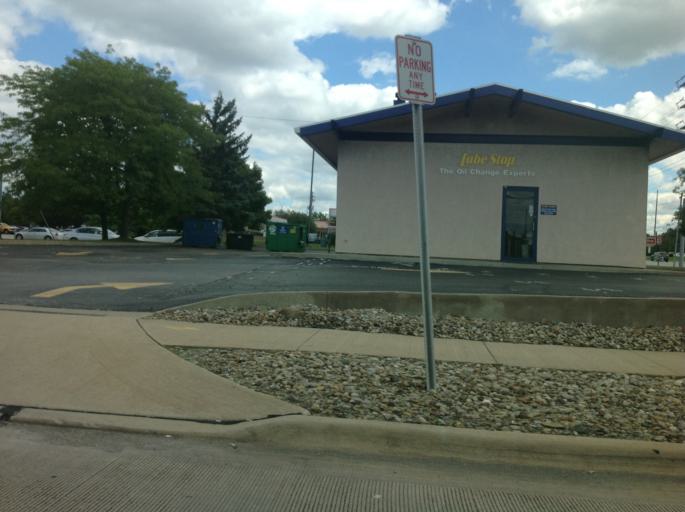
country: US
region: Ohio
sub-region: Cuyahoga County
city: Middleburg Heights
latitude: 41.3722
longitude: -81.8247
